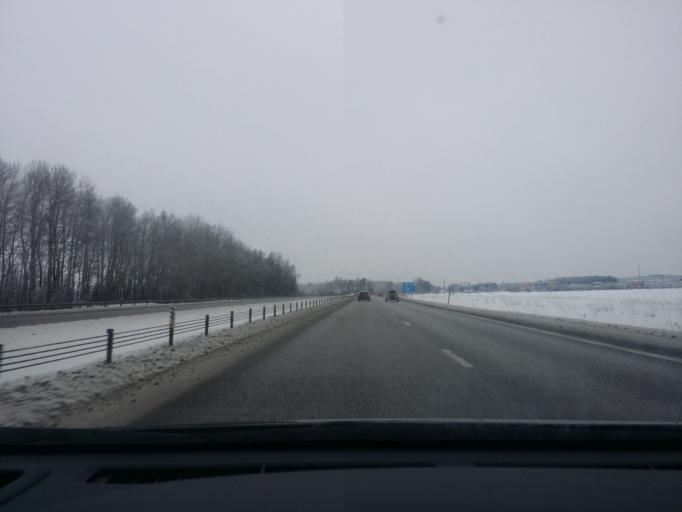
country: SE
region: OErebro
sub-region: Kumla Kommun
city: Kumla
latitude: 59.2030
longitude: 15.1271
